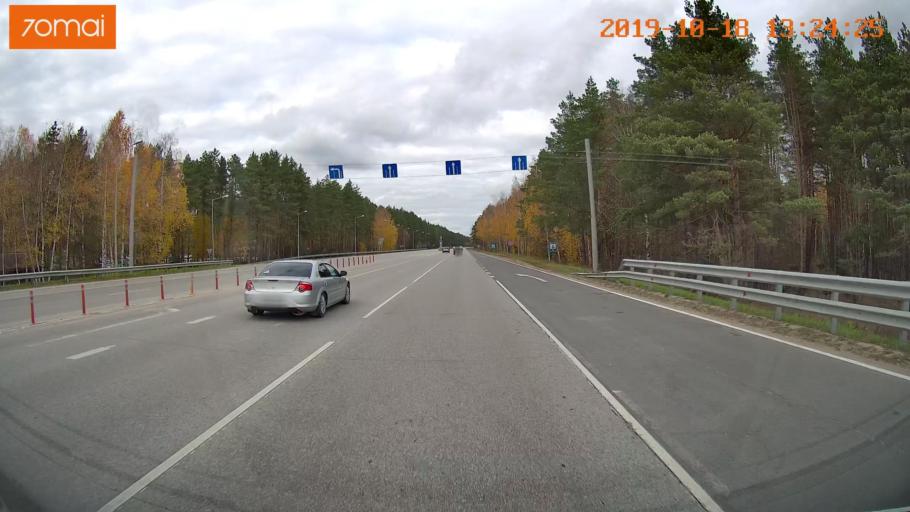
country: RU
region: Rjazan
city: Polyany
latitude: 54.7304
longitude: 39.8441
